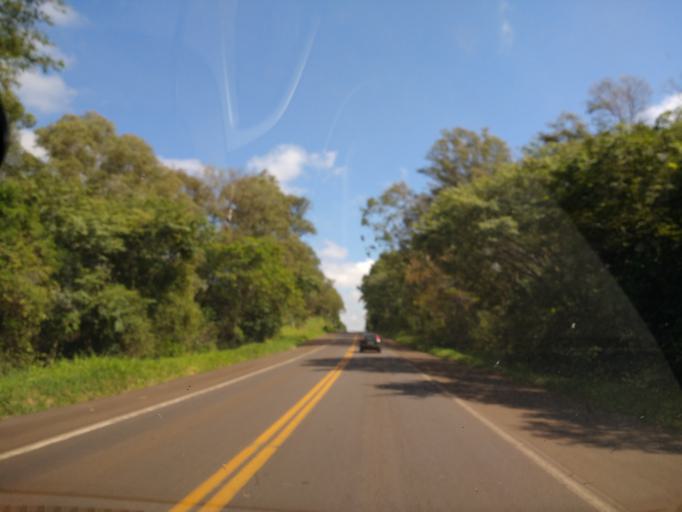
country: BR
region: Parana
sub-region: Umuarama
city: Umuarama
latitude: -23.7695
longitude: -53.2418
